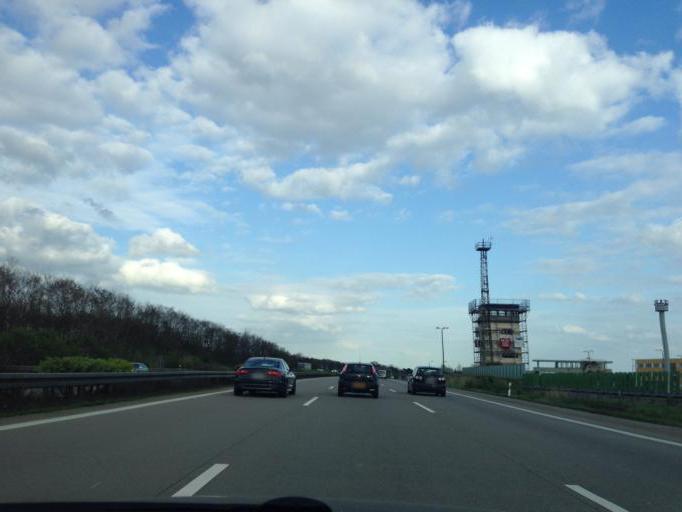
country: DE
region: Saxony-Anhalt
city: Beendorf
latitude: 52.2164
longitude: 11.0812
